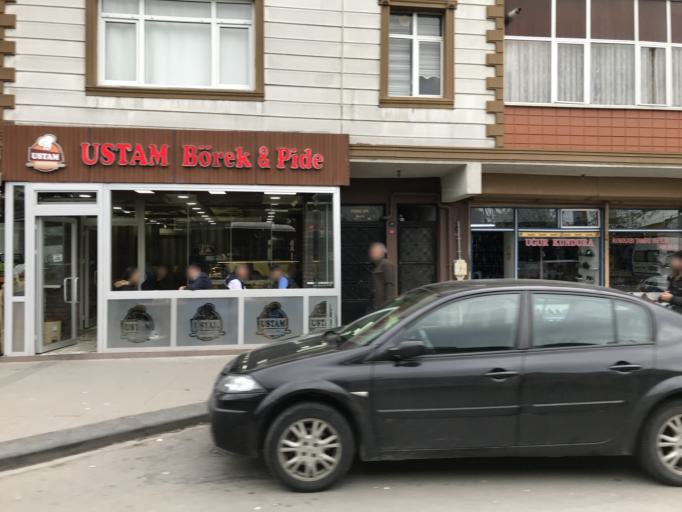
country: TR
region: Istanbul
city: Umraniye
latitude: 41.0125
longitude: 29.1663
